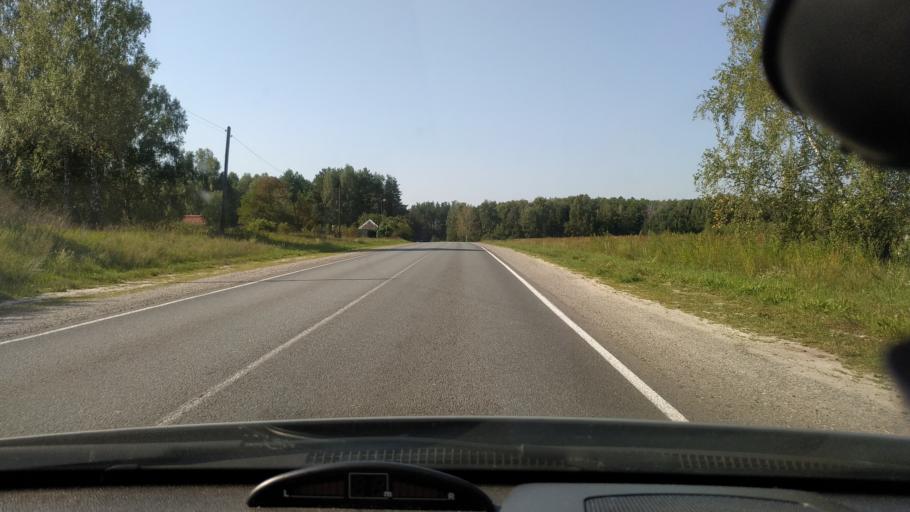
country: RU
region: Rjazan
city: Spas-Klepiki
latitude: 55.1043
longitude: 40.0819
